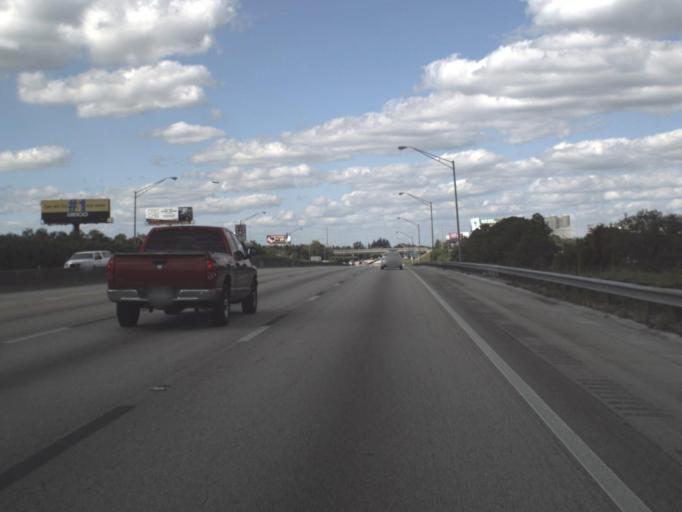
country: US
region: Florida
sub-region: Broward County
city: Davie
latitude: 26.0391
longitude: -80.2138
